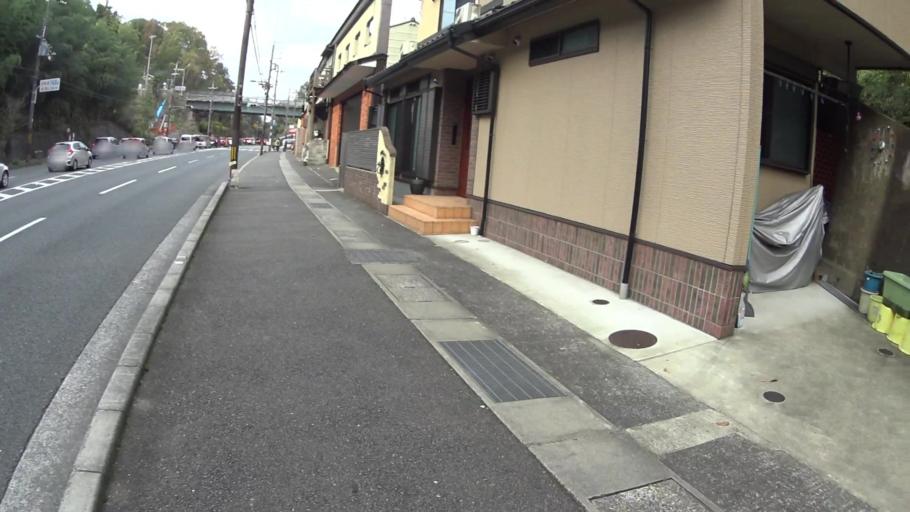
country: JP
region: Kyoto
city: Kyoto
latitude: 35.0014
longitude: 135.7910
